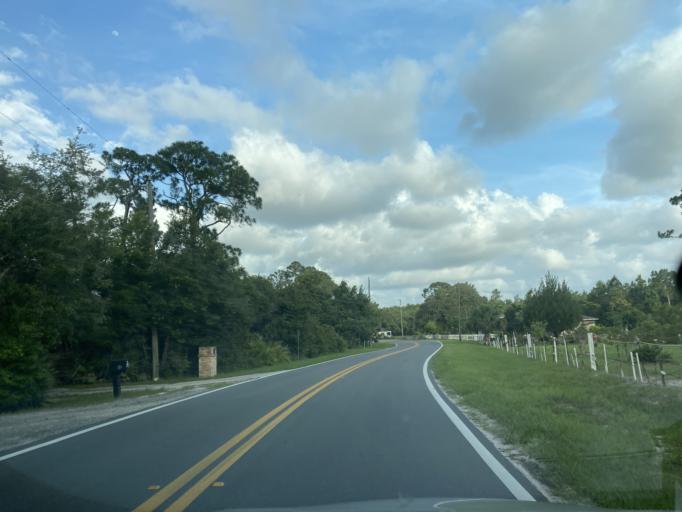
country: US
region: Florida
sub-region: Seminole County
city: Midway
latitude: 28.8468
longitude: -81.1737
